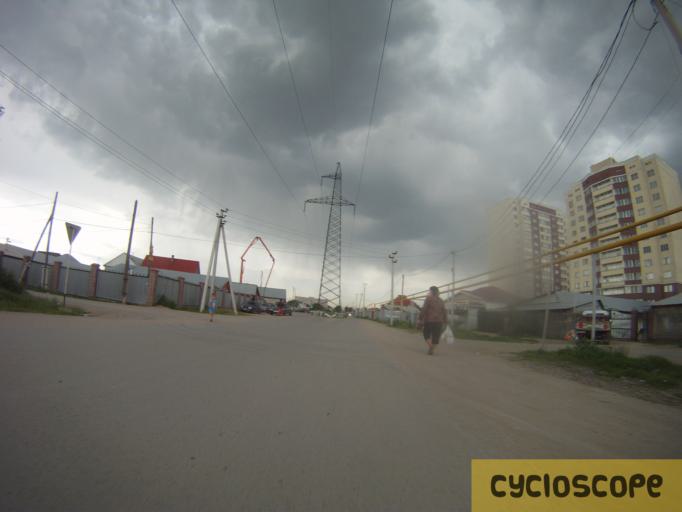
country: KZ
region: Almaty Qalasy
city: Almaty
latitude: 43.2247
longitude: 76.7921
